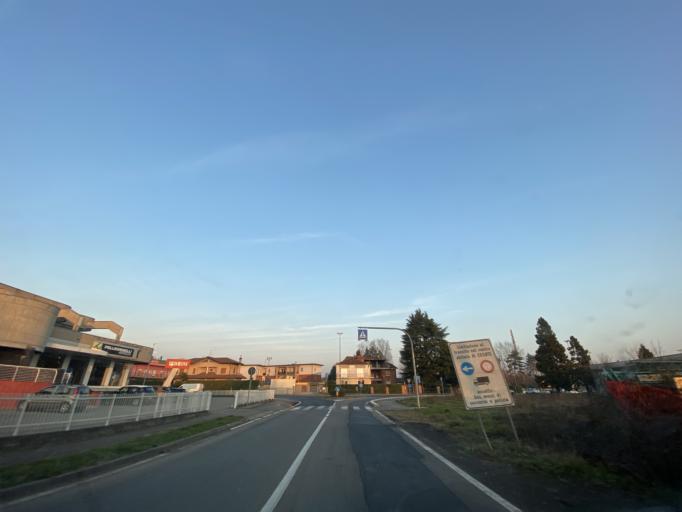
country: IT
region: Lombardy
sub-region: Citta metropolitana di Milano
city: Cesate
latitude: 45.6019
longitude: 9.0780
